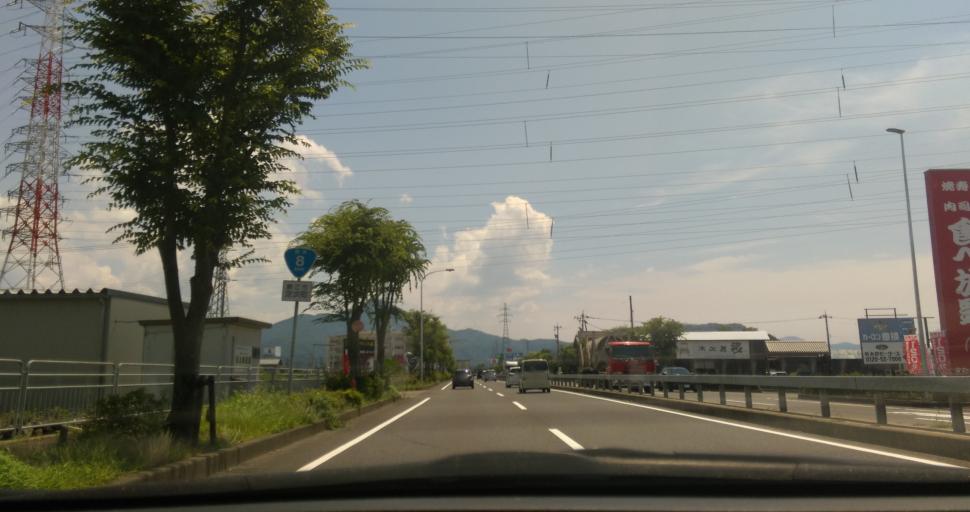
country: JP
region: Fukui
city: Sabae
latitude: 35.9314
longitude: 136.1899
